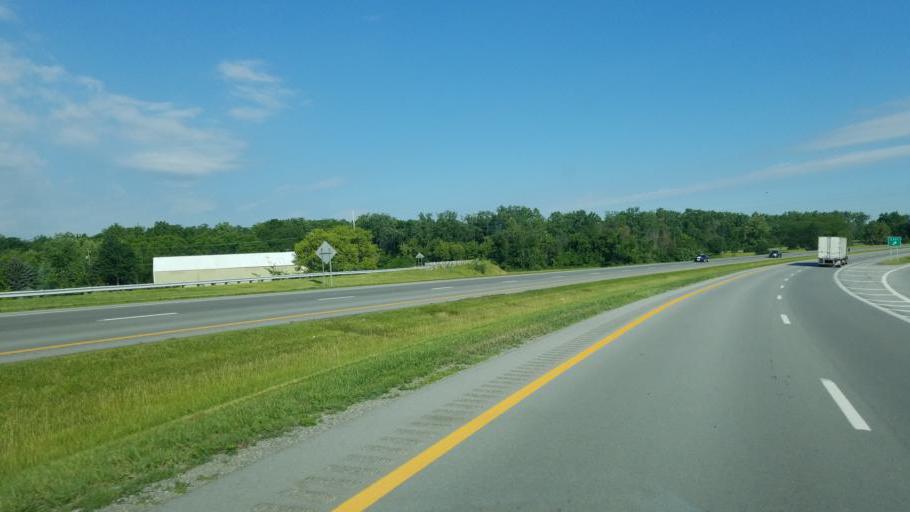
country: US
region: Ohio
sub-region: Hancock County
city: Findlay
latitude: 40.9880
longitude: -83.6478
